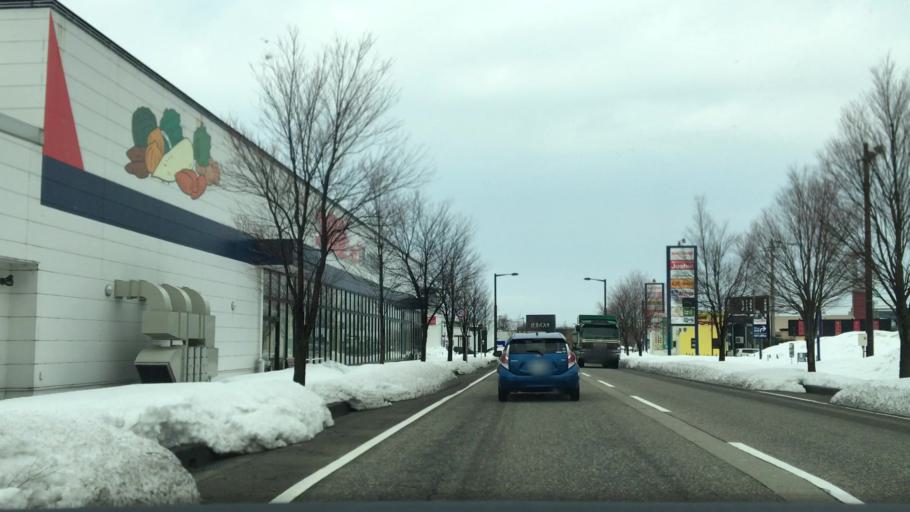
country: JP
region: Ishikawa
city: Nonoichi
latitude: 36.5163
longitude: 136.6091
